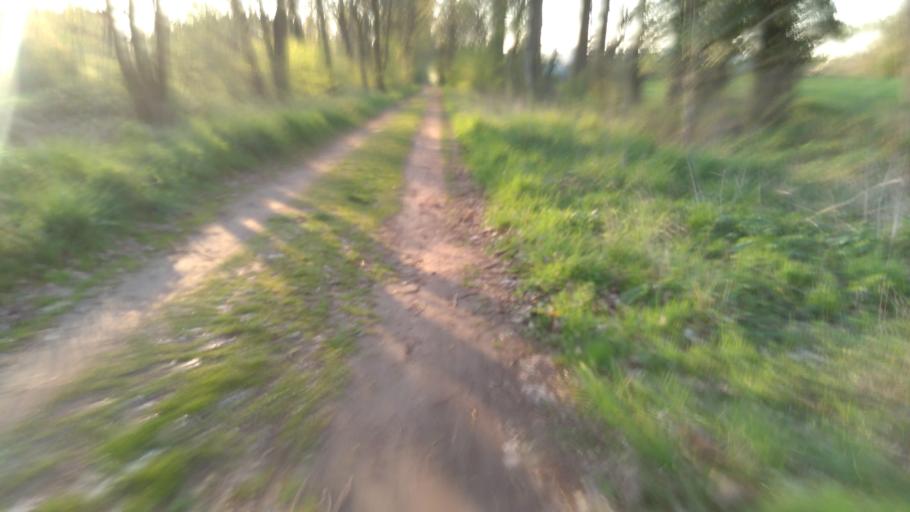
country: DE
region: Lower Saxony
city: Harsefeld
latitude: 53.4681
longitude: 9.5031
